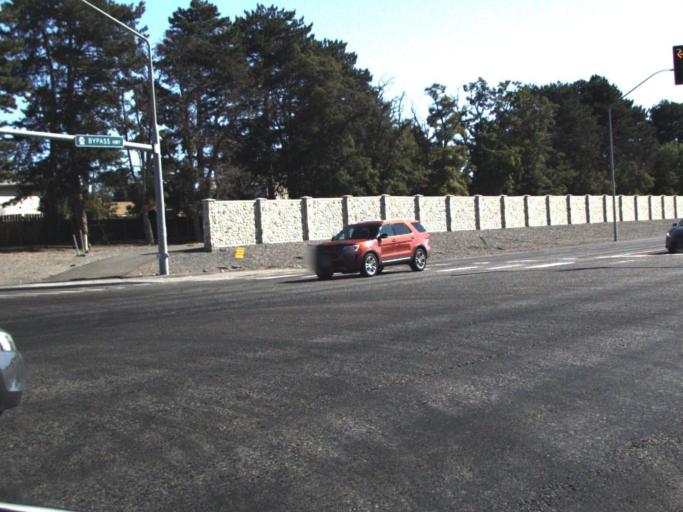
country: US
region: Washington
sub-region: Benton County
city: Richland
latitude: 46.2676
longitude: -119.3021
